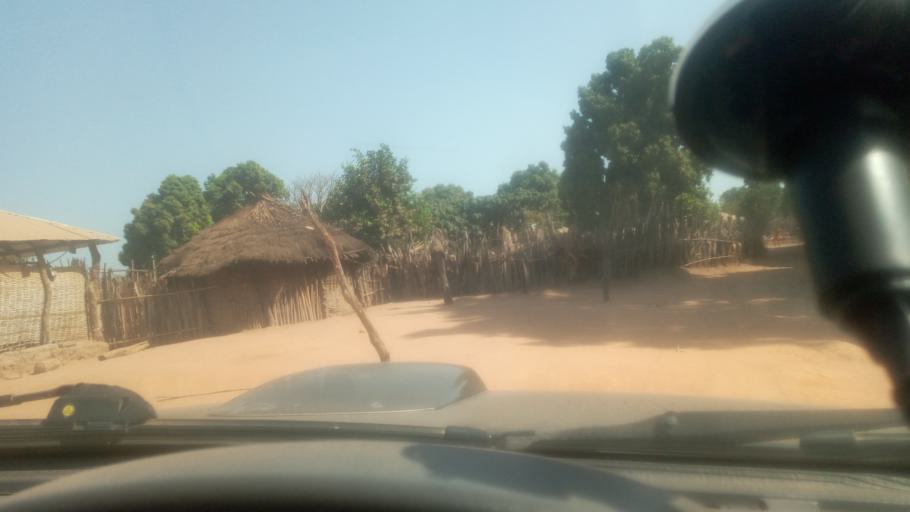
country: GW
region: Oio
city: Farim
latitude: 12.4620
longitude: -15.4070
